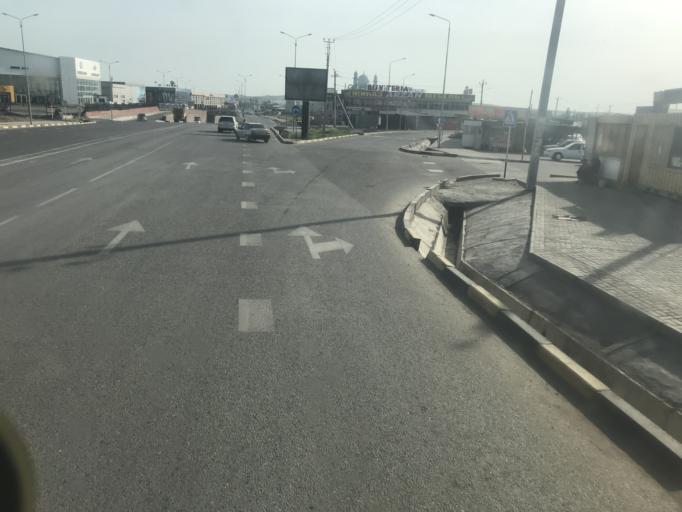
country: KZ
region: Ongtustik Qazaqstan
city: Shymkent
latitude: 42.3547
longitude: 69.5327
